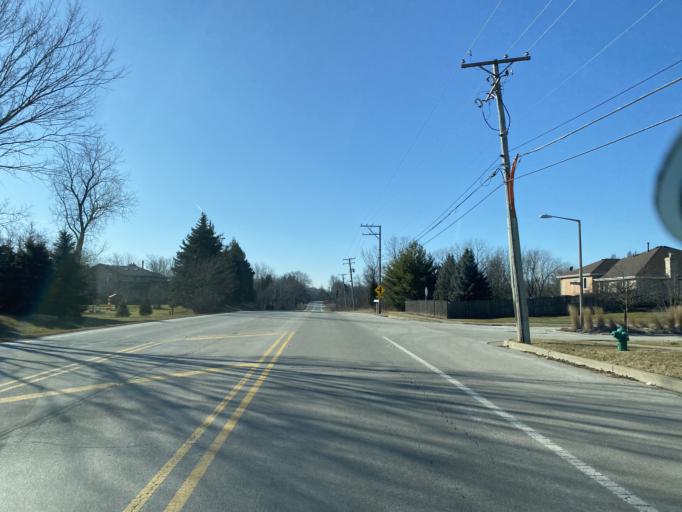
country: US
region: Illinois
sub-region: Cook County
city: Lemont
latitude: 41.6538
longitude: -87.9782
